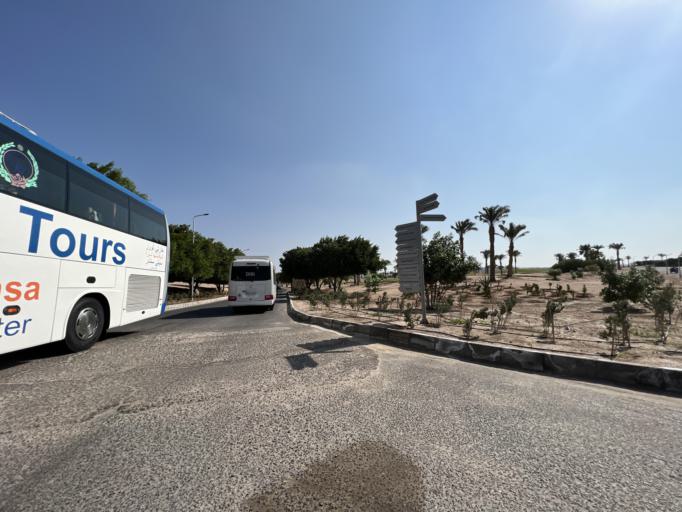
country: EG
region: Red Sea
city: Makadi Bay
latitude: 26.9855
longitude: 33.8877
